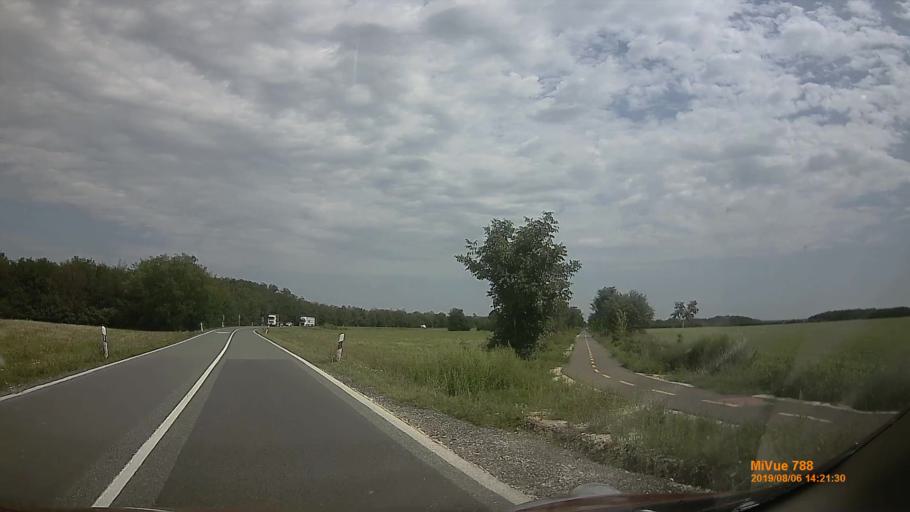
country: HU
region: Vas
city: Vep
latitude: 47.1695
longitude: 16.7763
